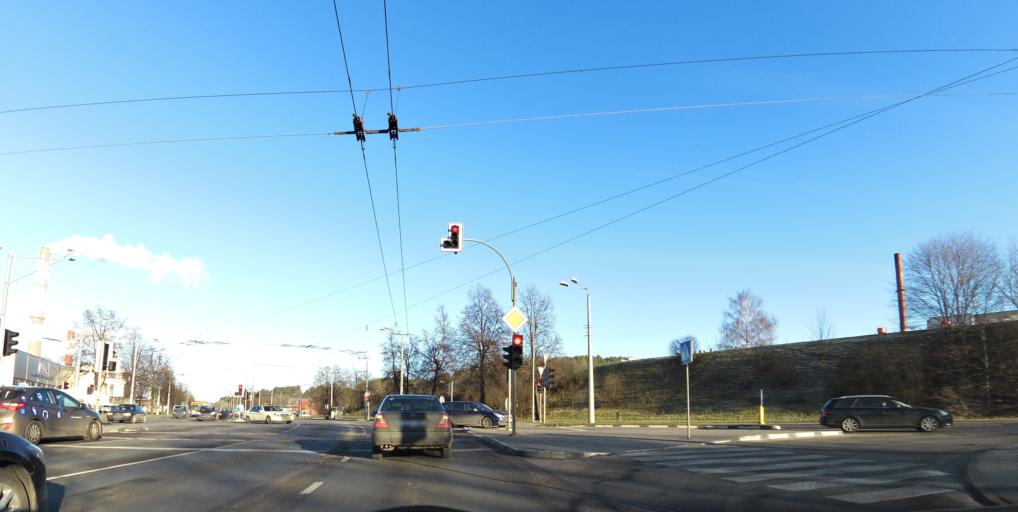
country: LT
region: Vilnius County
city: Vilkpede
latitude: 54.6588
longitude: 25.2327
